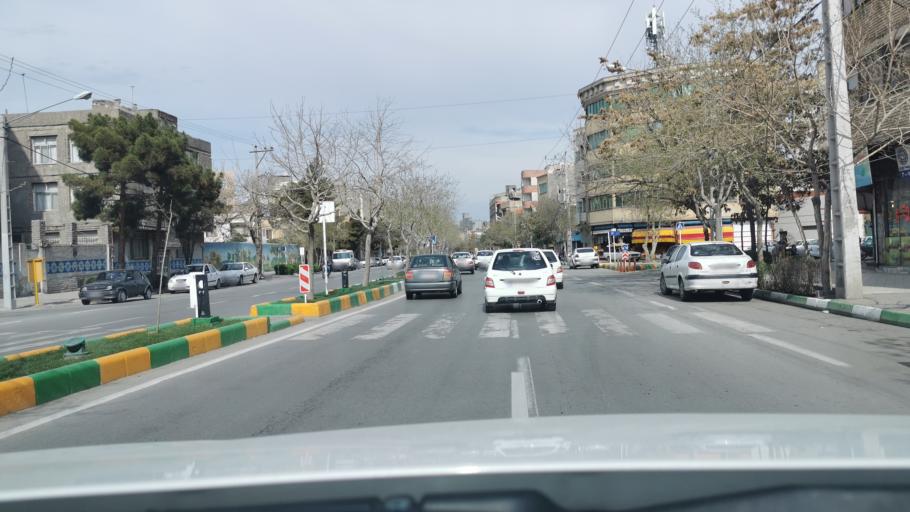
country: IR
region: Razavi Khorasan
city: Mashhad
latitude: 36.3177
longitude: 59.6000
